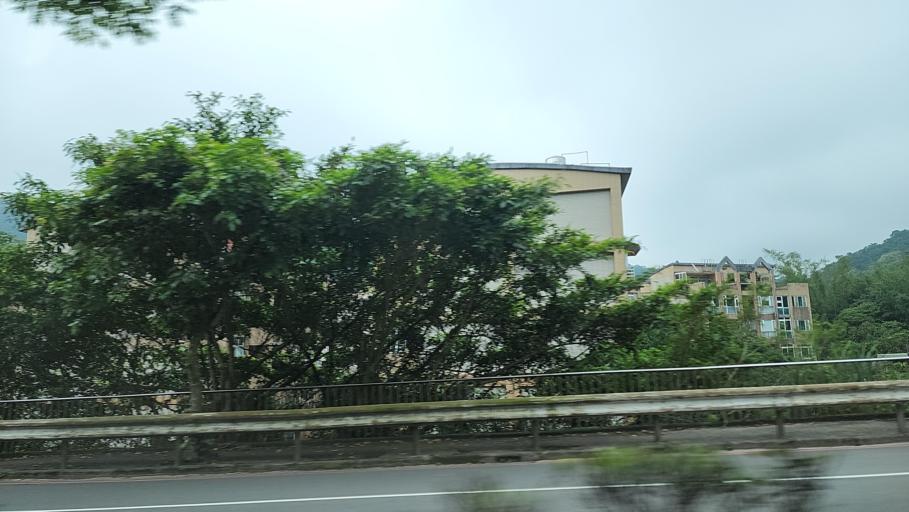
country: TW
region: Taiwan
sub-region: Keelung
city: Keelung
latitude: 25.1600
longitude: 121.6946
